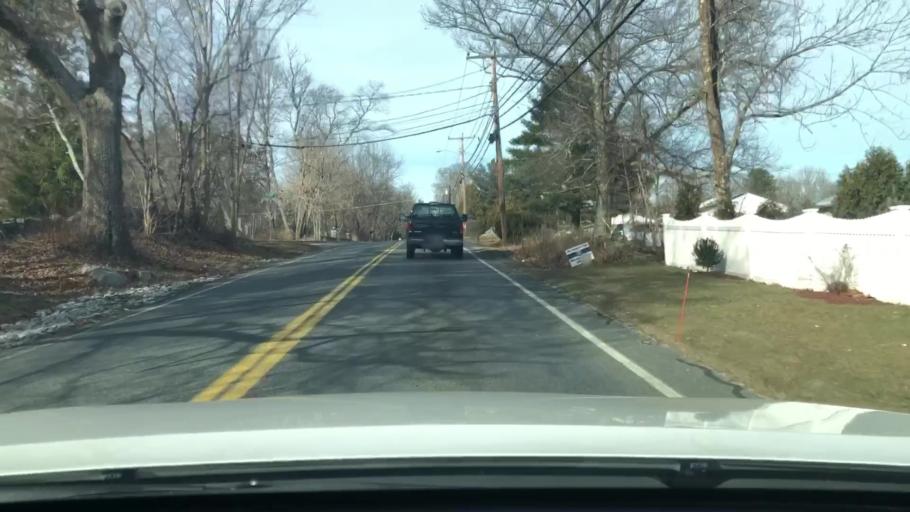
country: US
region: Massachusetts
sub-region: Worcester County
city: Mendon
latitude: 42.0885
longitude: -71.5326
